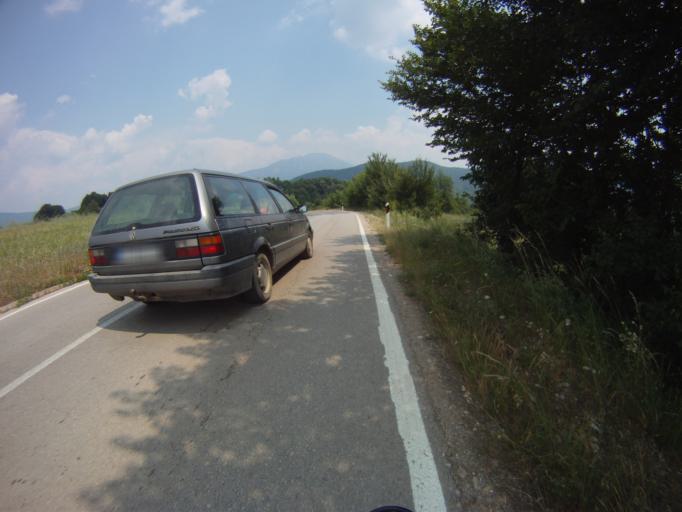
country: RS
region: Central Serbia
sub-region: Nisavski Okrug
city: Gadzin Han
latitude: 43.2067
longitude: 22.0127
